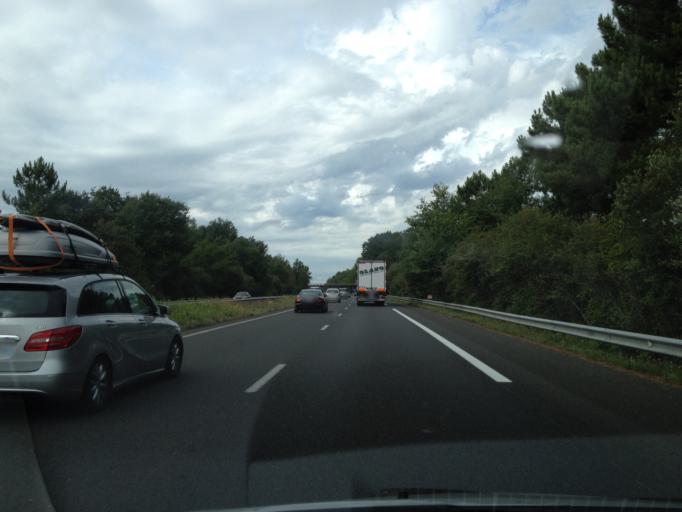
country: FR
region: Aquitaine
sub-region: Departement de la Gironde
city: Castets-en-Dorthe
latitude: 44.5319
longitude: -0.1781
